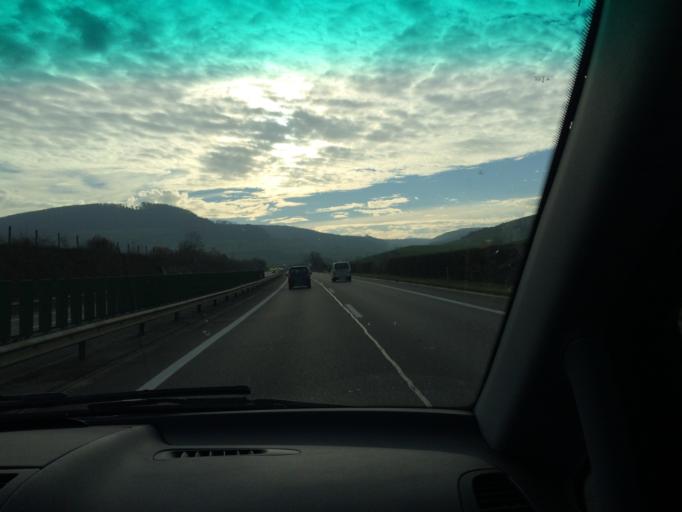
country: CH
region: Basel-Landschaft
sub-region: Bezirk Liestal
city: Arisdorf
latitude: 47.5163
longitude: 7.7560
